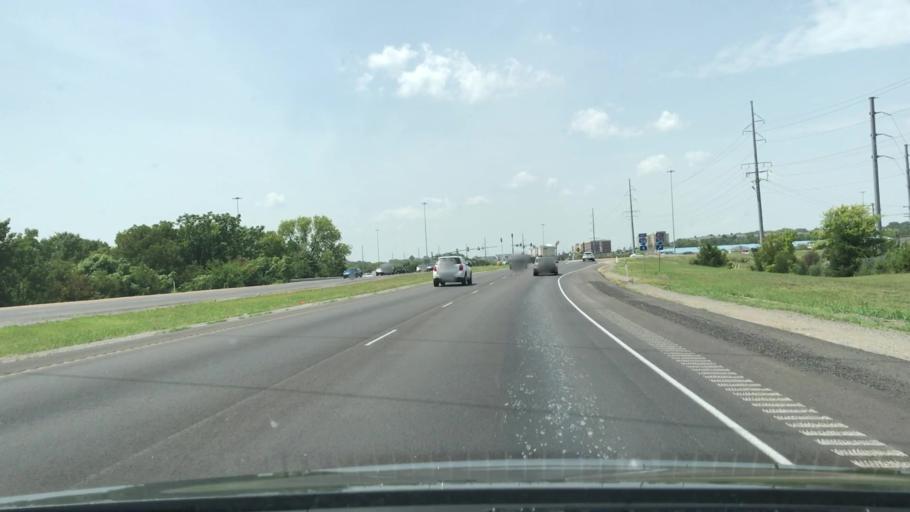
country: US
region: Tennessee
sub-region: Rutherford County
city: La Vergne
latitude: 35.9769
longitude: -86.5663
